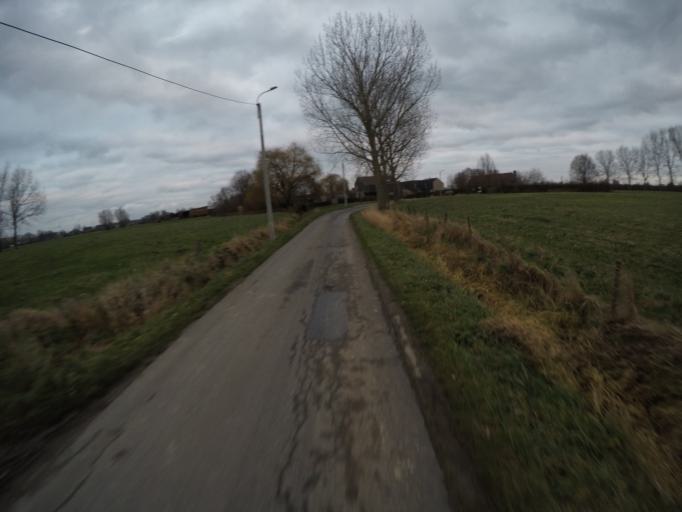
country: BE
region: Flanders
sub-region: Provincie Oost-Vlaanderen
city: Sint-Gillis-Waas
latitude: 51.2236
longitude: 4.1791
